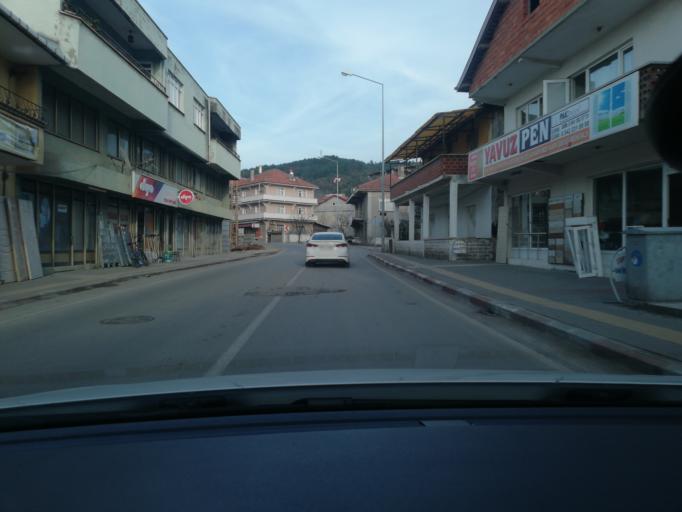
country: TR
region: Zonguldak
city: Tieum
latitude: 41.5614
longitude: 32.0263
